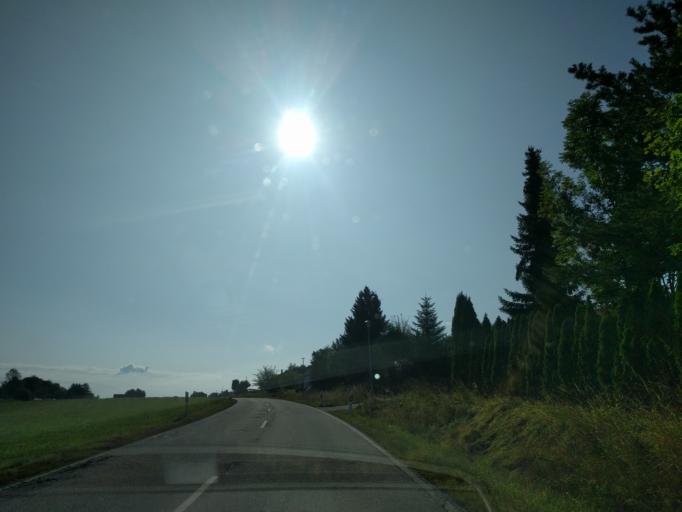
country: DE
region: Bavaria
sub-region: Lower Bavaria
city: Hohenau
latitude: 48.8605
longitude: 13.4973
